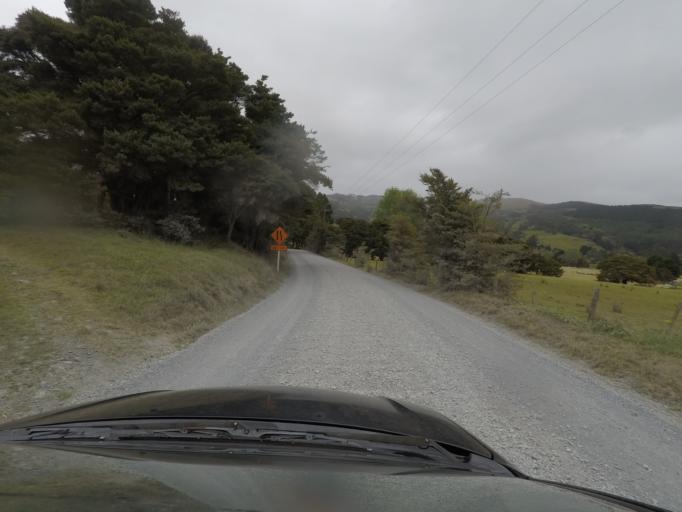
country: NZ
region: Auckland
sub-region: Auckland
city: Warkworth
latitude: -36.2596
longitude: 174.7242
